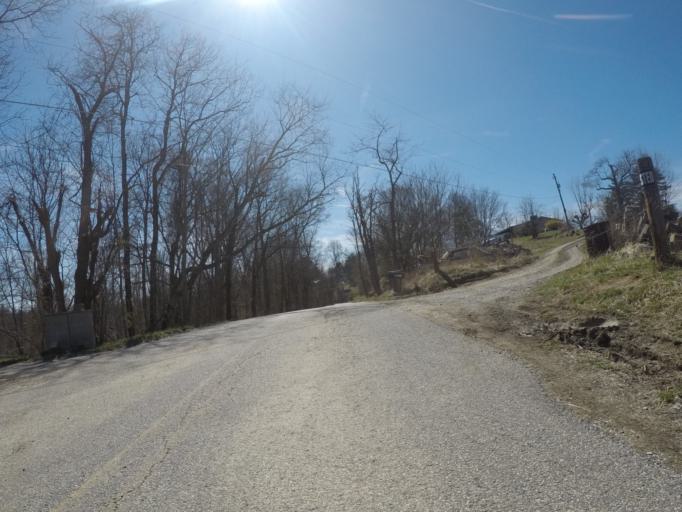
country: US
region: West Virginia
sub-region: Cabell County
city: Huntington
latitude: 38.4455
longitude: -82.4871
